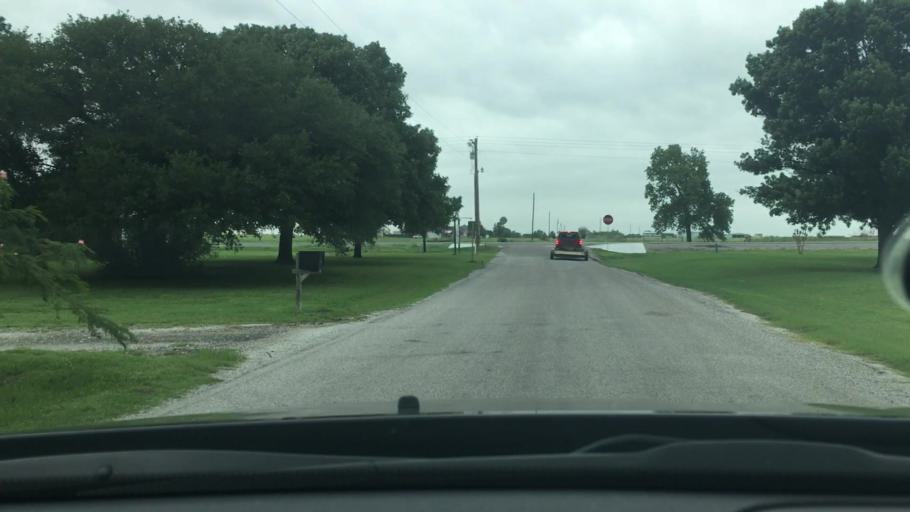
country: US
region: Oklahoma
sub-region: Love County
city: Marietta
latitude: 33.9395
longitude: -97.1608
